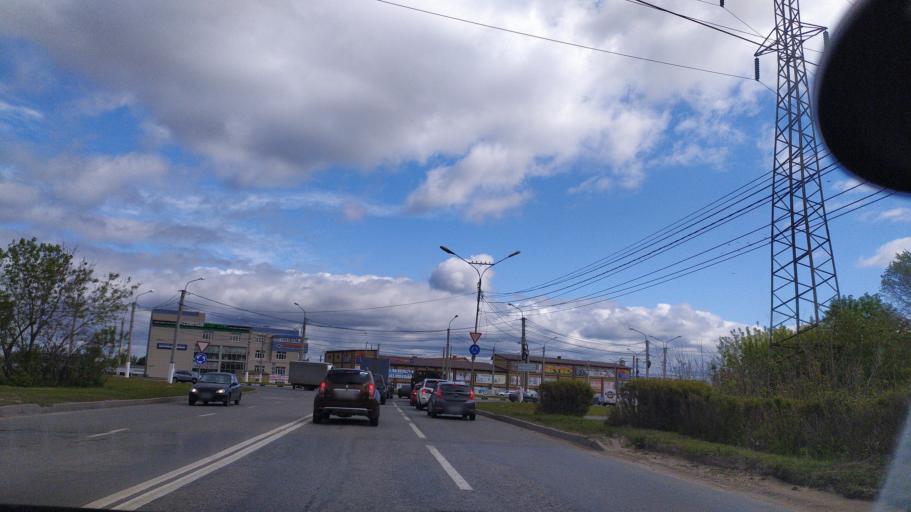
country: RU
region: Chuvashia
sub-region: Cheboksarskiy Rayon
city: Cheboksary
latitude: 56.1272
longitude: 47.3097
